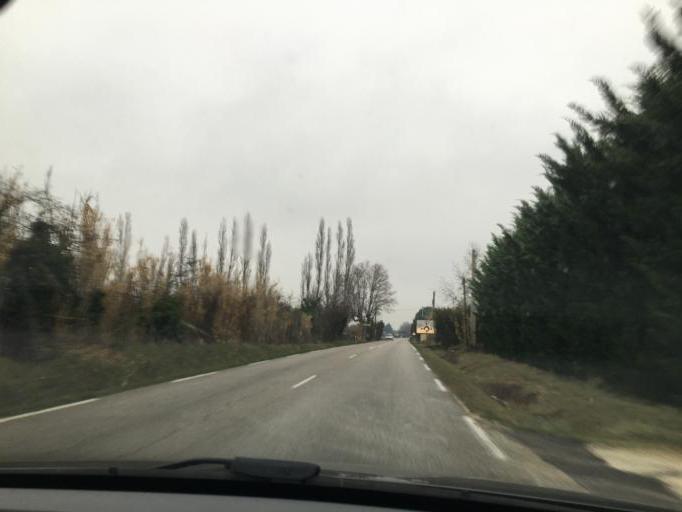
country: FR
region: Provence-Alpes-Cote d'Azur
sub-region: Departement du Vaucluse
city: Lagnes
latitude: 43.8906
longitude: 5.0943
